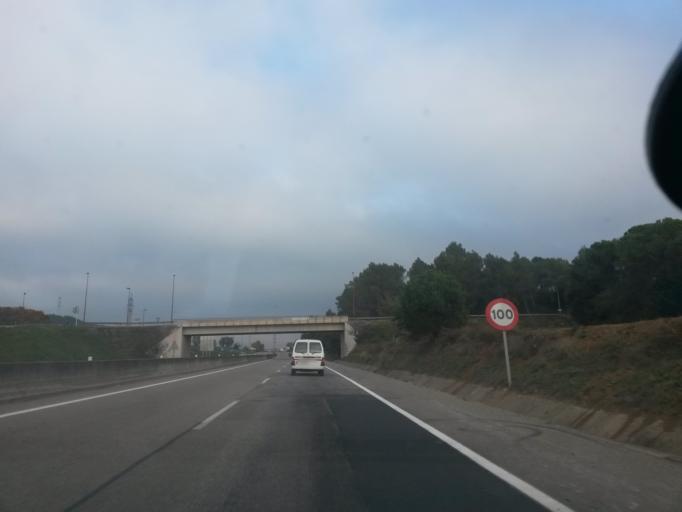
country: ES
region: Catalonia
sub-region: Provincia de Girona
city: Sarria de Ter
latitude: 42.0412
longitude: 2.8220
